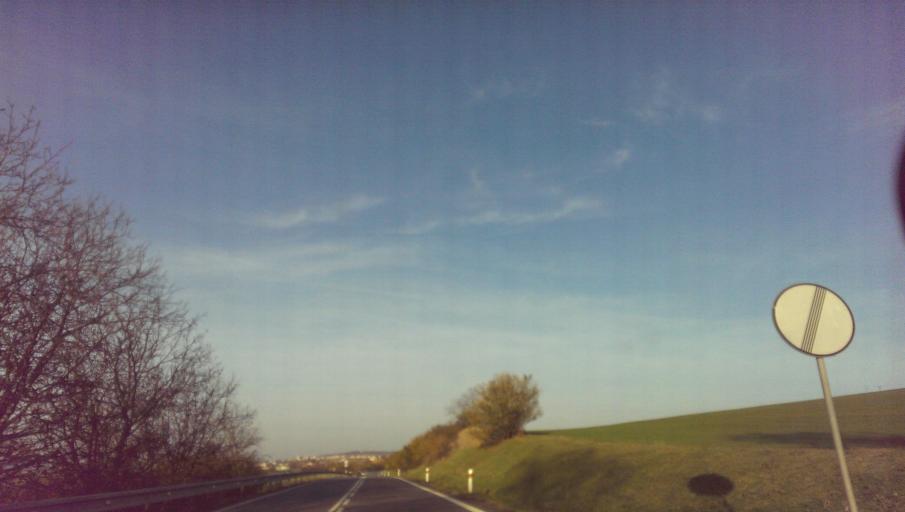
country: CZ
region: Zlin
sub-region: Okres Zlin
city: Ostrozska Nova Ves
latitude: 49.0212
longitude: 17.4506
